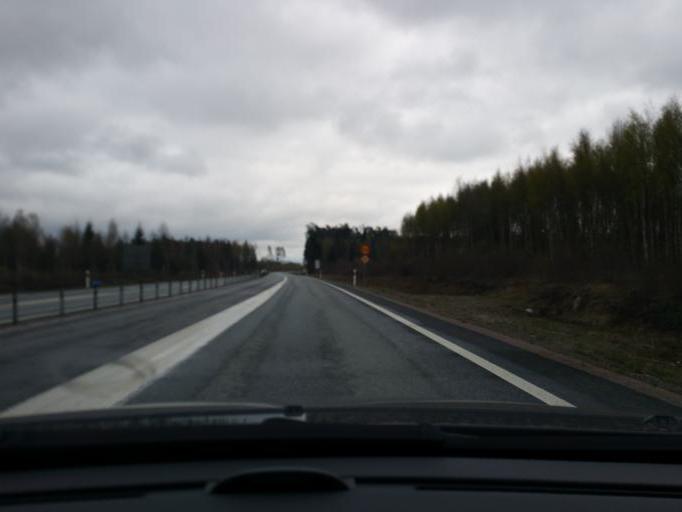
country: SE
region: Kronoberg
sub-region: Vaxjo Kommun
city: Vaexjoe
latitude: 56.9107
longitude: 14.7220
